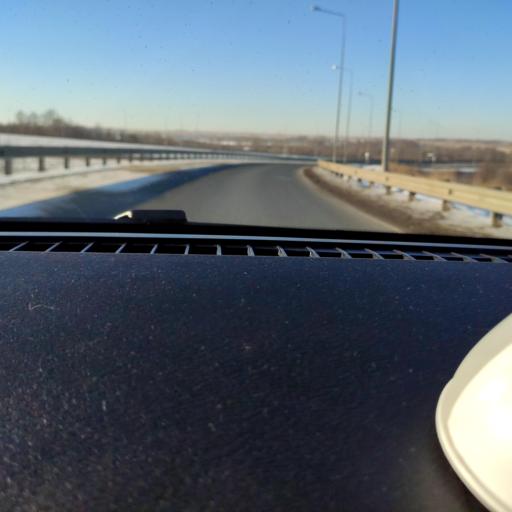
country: RU
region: Samara
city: Smyshlyayevka
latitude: 53.1367
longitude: 50.4288
